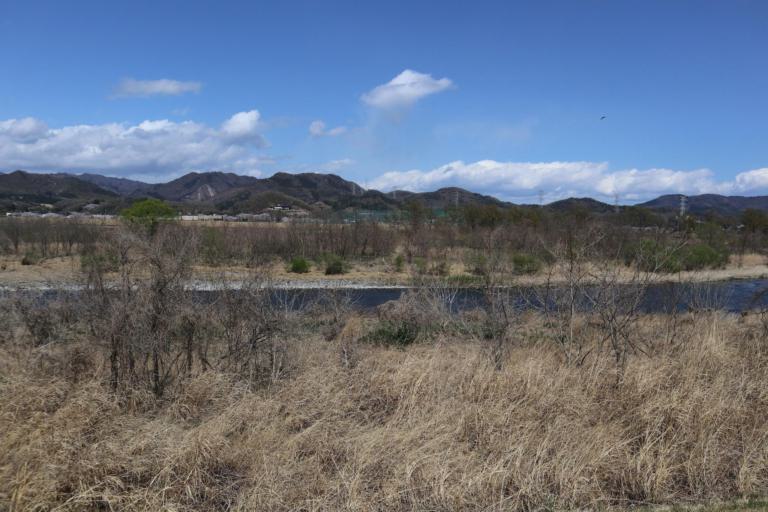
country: JP
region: Gunma
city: Kiryu
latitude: 36.3684
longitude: 139.3643
